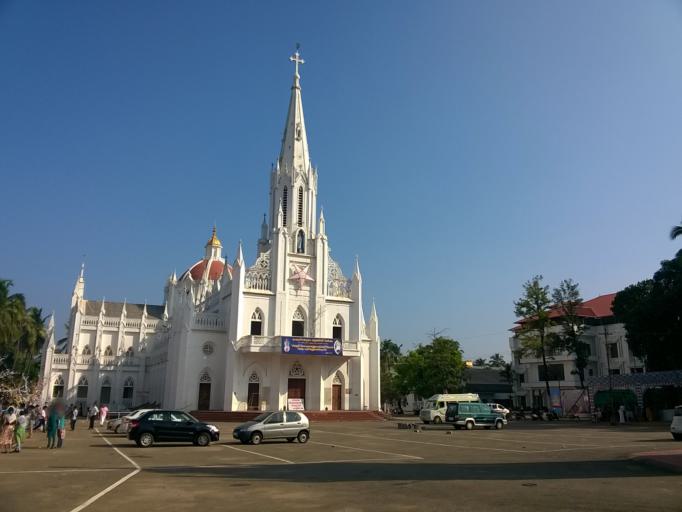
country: IN
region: Kerala
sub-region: Thrissur District
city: Trichur
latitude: 10.5224
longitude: 76.2273
